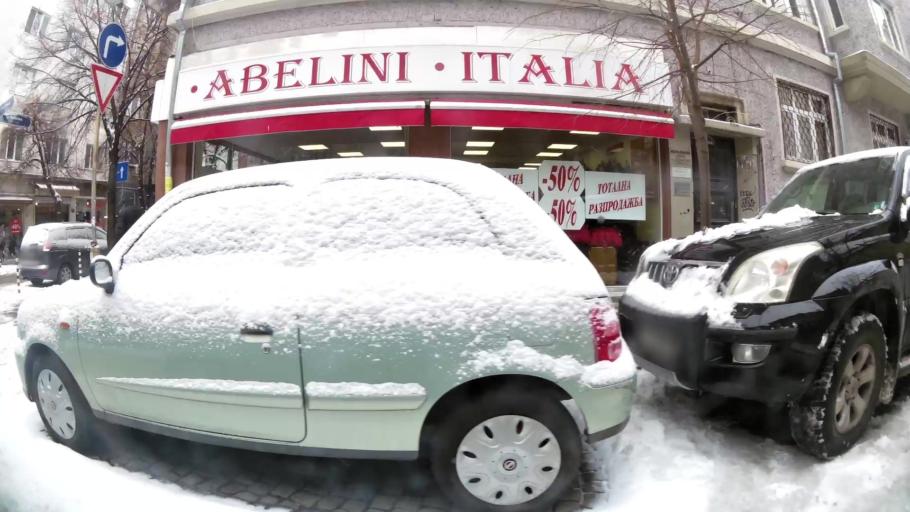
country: BG
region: Sofia-Capital
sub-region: Stolichna Obshtina
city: Sofia
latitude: 42.6932
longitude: 23.3166
